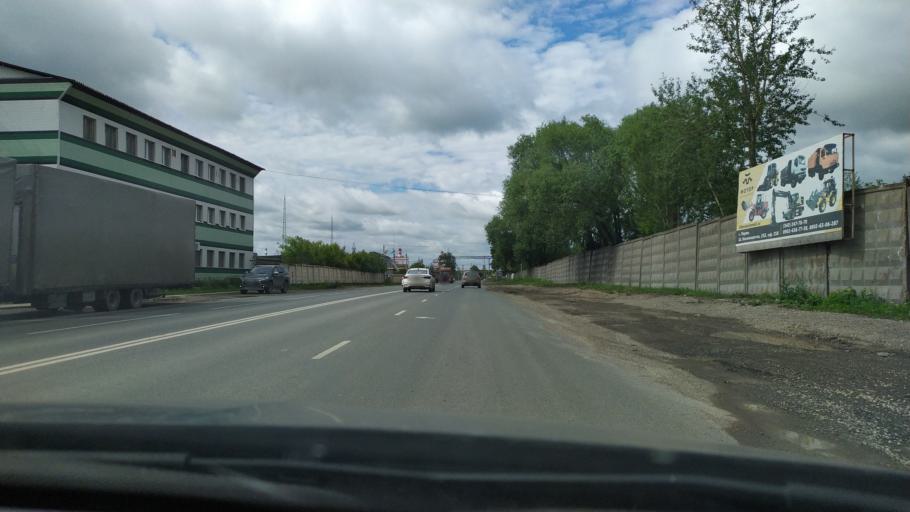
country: RU
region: Perm
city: Kondratovo
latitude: 57.9303
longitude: 56.1458
